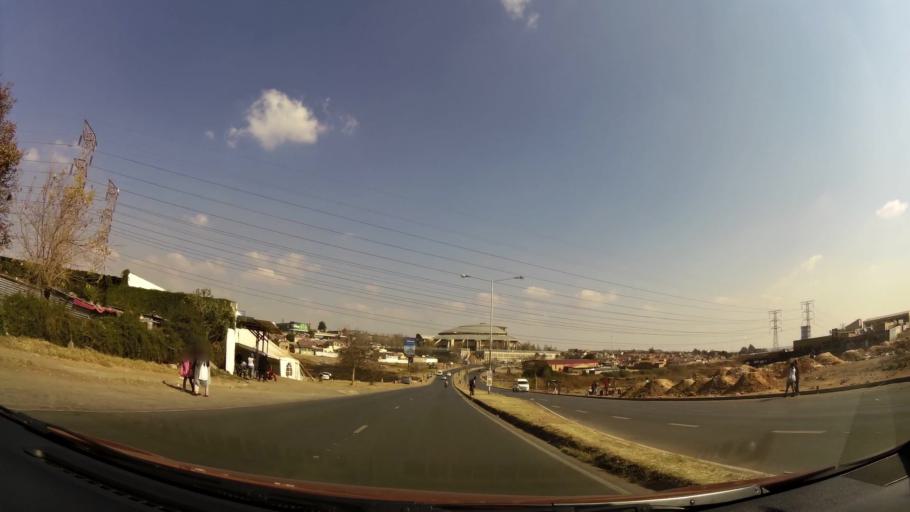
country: ZA
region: Gauteng
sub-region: City of Johannesburg Metropolitan Municipality
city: Soweto
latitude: -26.2540
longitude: 27.9451
